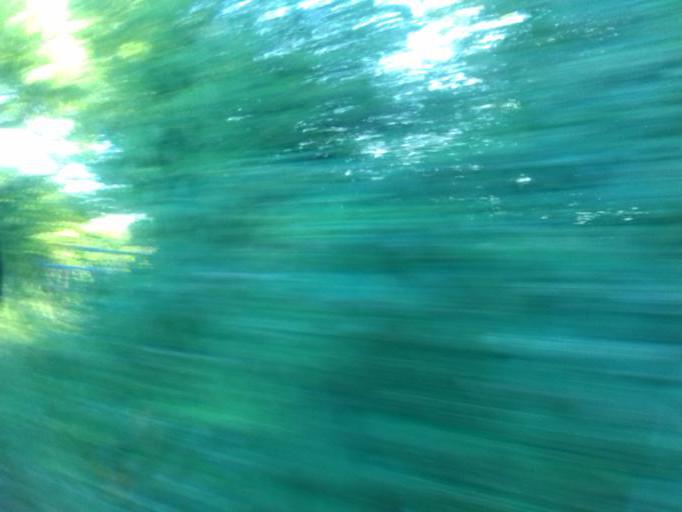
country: IE
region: Leinster
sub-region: Fingal County
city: Blanchardstown
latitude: 53.4322
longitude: -6.3611
